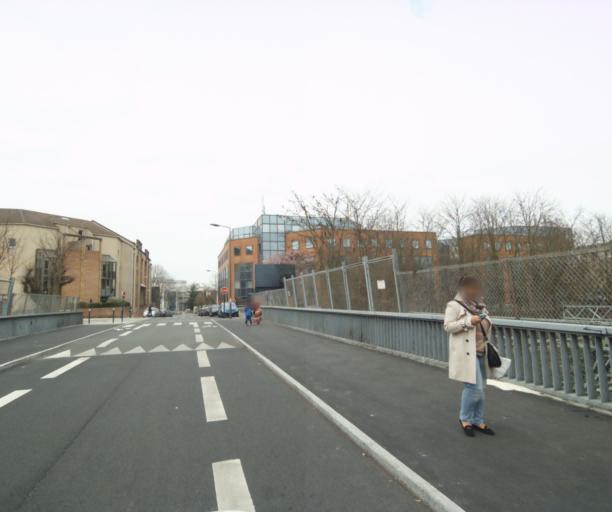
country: FR
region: Ile-de-France
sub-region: Departement du Val-d'Oise
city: Vaureal
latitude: 49.0494
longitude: 2.0356
